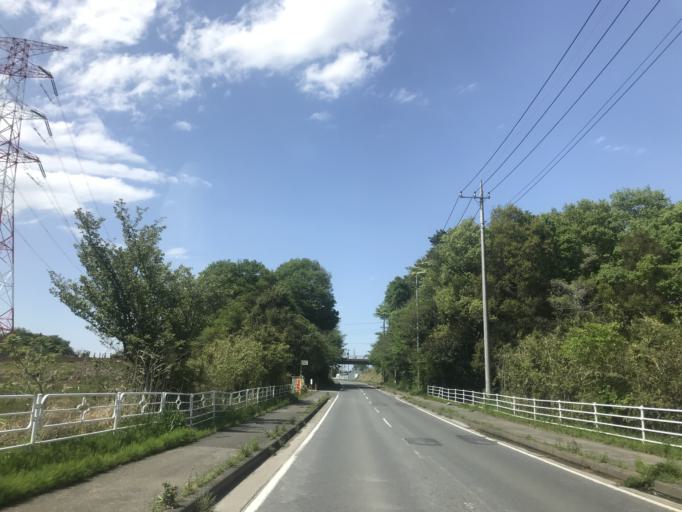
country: JP
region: Chiba
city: Noda
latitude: 35.9591
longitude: 139.9090
